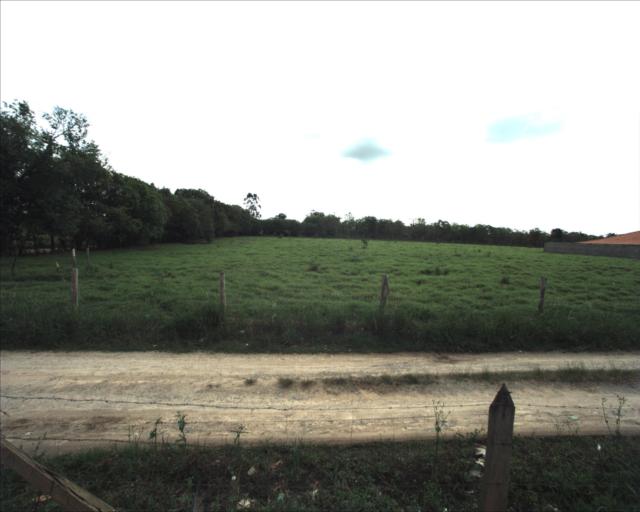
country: BR
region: Sao Paulo
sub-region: Aracoiaba Da Serra
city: Aracoiaba da Serra
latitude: -23.5520
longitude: -47.5458
